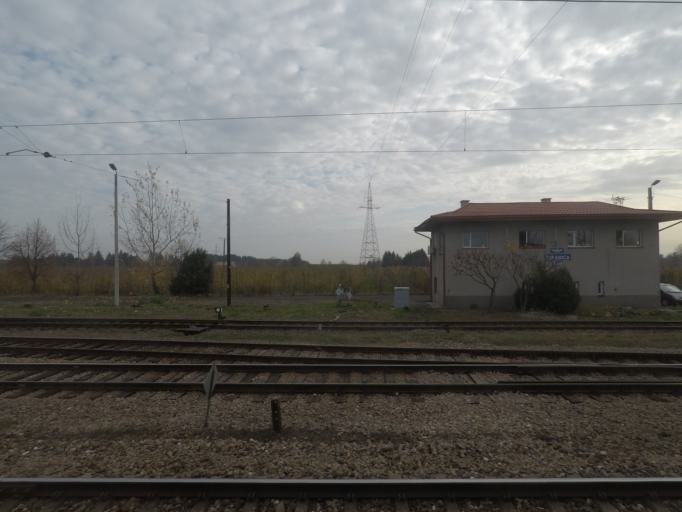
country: PL
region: Subcarpathian Voivodeship
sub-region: Powiat przemyski
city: Zurawica
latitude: 49.8231
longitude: 22.8306
